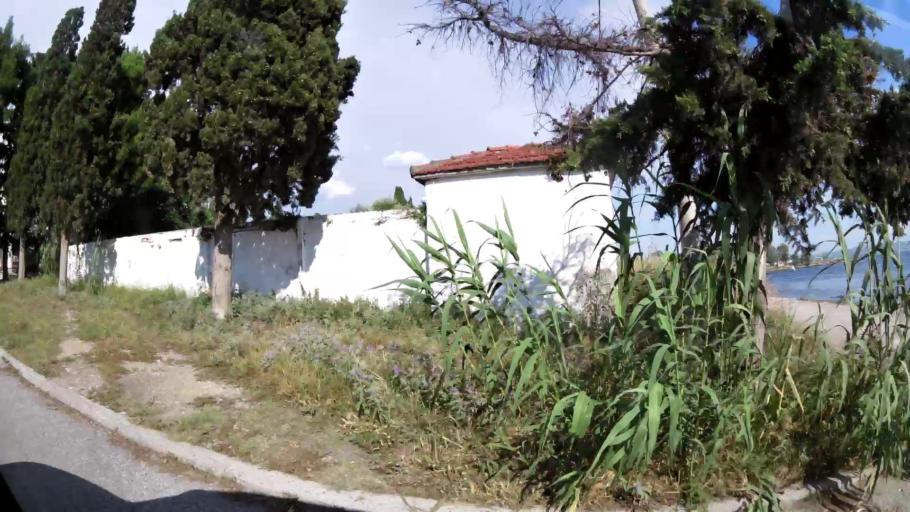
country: GR
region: Central Macedonia
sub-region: Nomos Thessalonikis
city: Kalamaria
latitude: 40.5653
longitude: 22.9596
